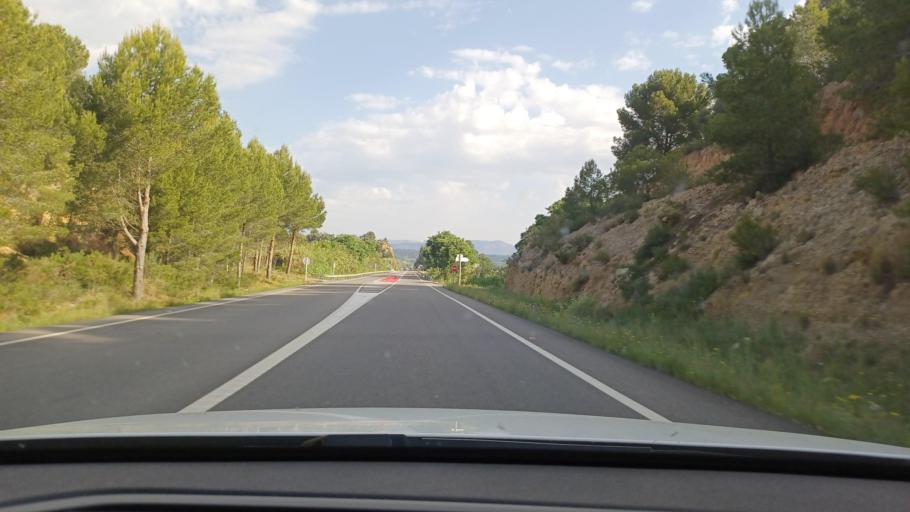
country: ES
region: Catalonia
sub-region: Provincia de Tarragona
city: Tivenys
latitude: 40.8887
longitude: 0.4911
